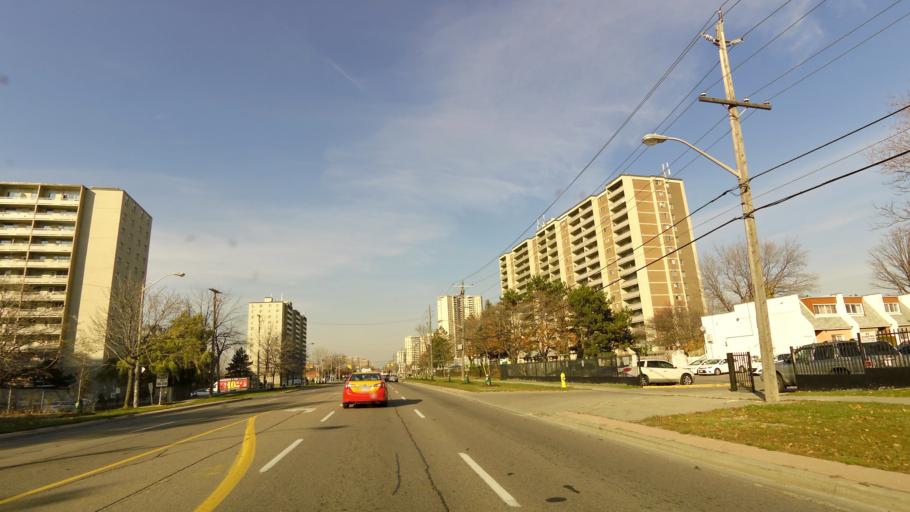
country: CA
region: Ontario
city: Concord
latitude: 43.7531
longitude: -79.5166
